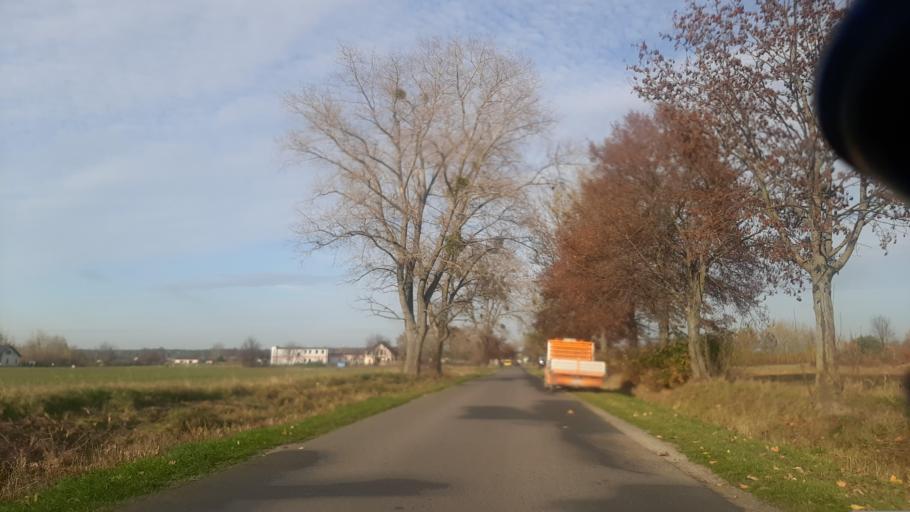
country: PL
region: Lublin Voivodeship
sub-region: Powiat lubelski
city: Garbow
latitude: 51.3952
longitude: 22.3306
